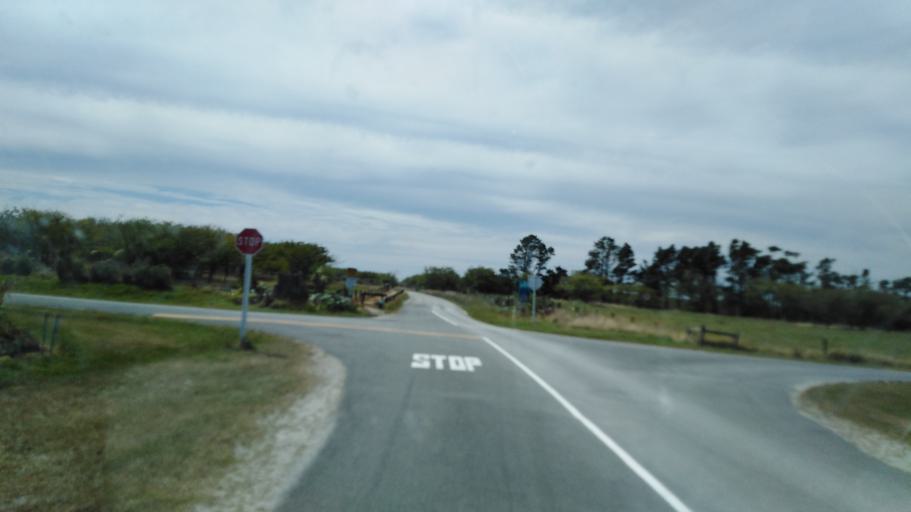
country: NZ
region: West Coast
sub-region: Buller District
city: Westport
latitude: -41.7388
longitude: 171.6039
